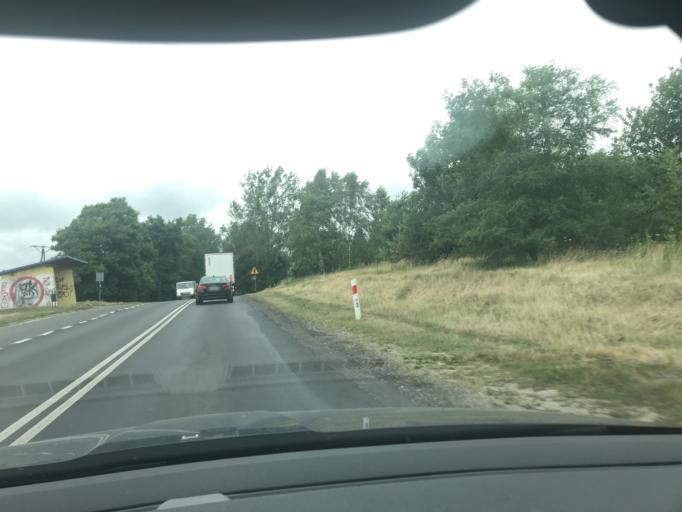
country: PL
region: Lodz Voivodeship
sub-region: Powiat zgierski
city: Zgierz
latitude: 51.8938
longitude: 19.4214
